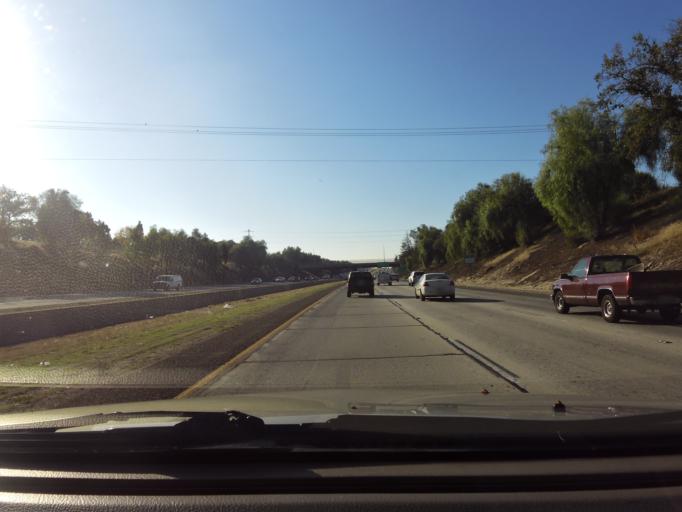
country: US
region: California
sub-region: Fresno County
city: Fresno
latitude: 36.7895
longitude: -119.7845
